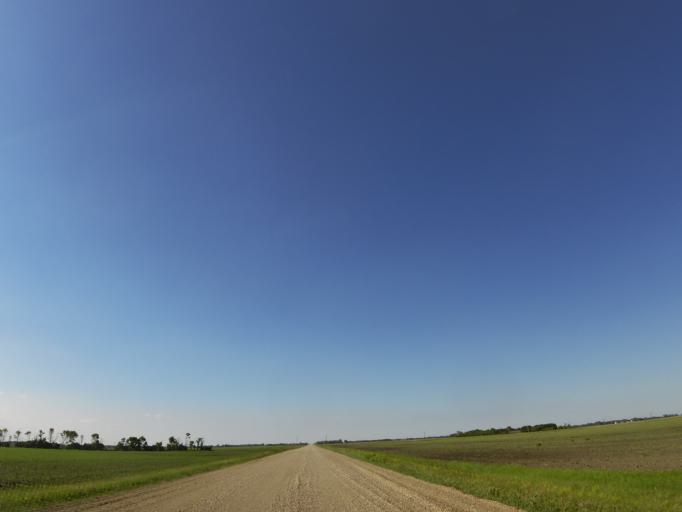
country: US
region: North Dakota
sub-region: Walsh County
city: Grafton
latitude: 48.4055
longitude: -97.2778
